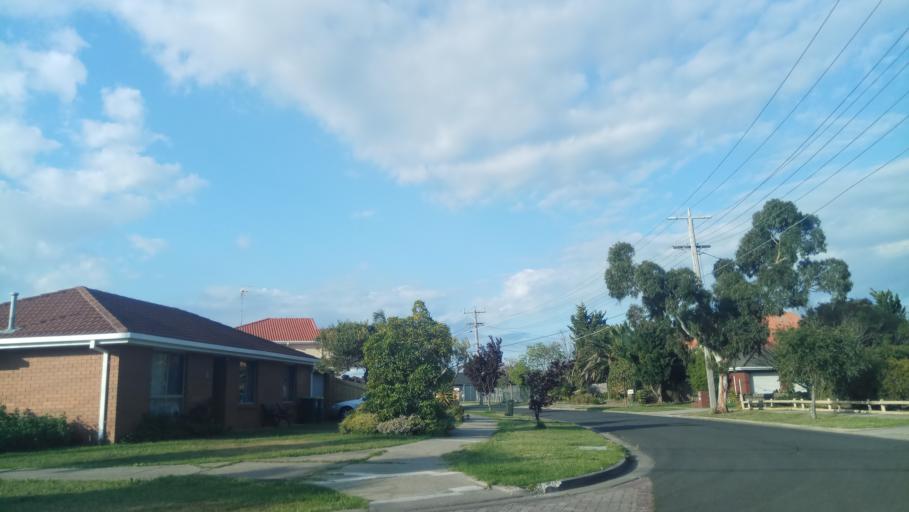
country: AU
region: Victoria
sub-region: Hobsons Bay
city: Altona Meadows
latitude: -37.8844
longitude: 144.7908
